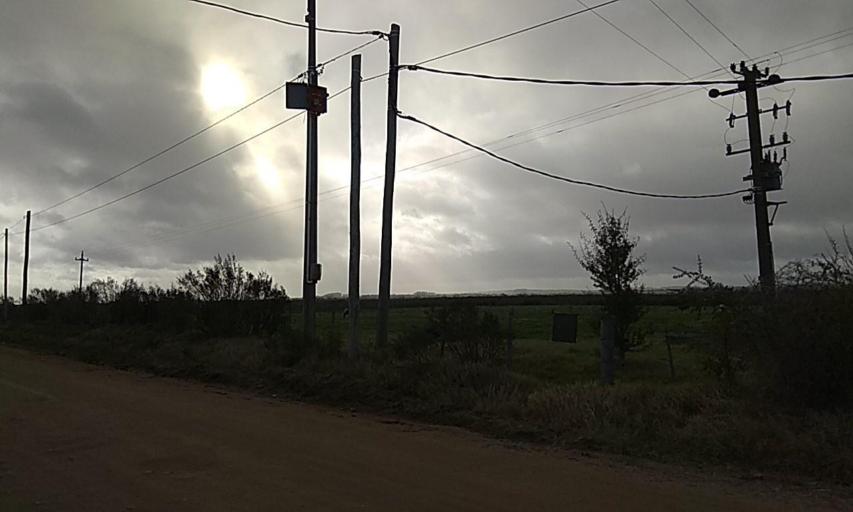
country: UY
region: Florida
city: Florida
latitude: -34.0744
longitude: -56.1979
